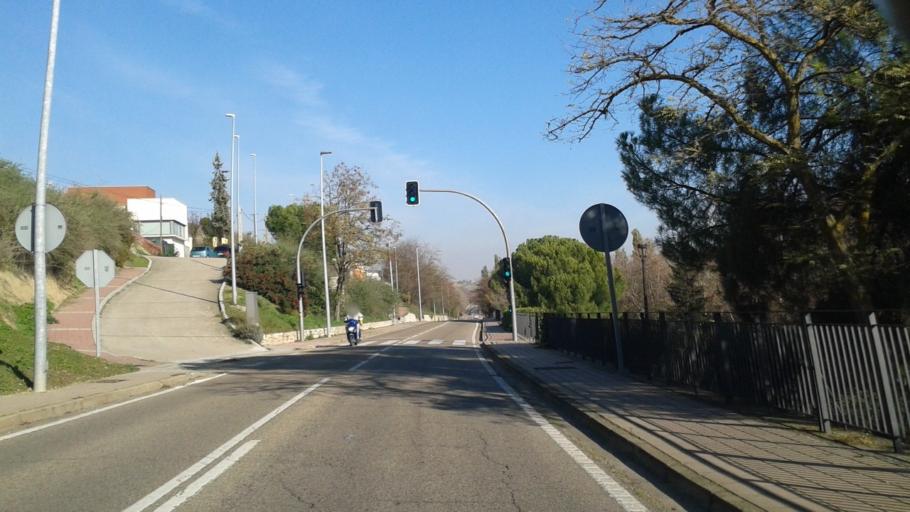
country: ES
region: Castille and Leon
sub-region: Provincia de Valladolid
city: Valladolid
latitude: 41.6644
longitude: -4.7399
